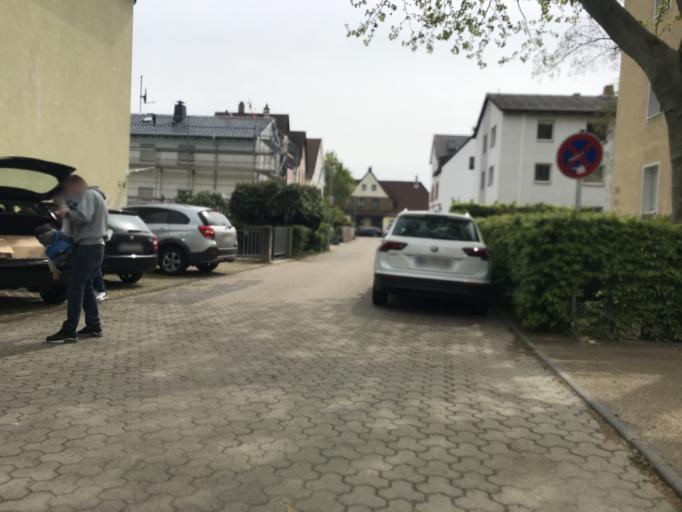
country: DE
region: Hesse
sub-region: Regierungsbezirk Darmstadt
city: Hochheim am Main
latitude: 49.9969
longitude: 8.3244
